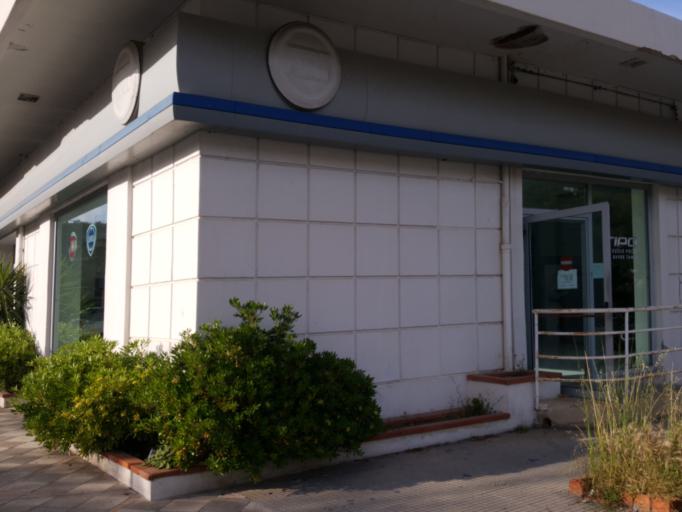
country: IT
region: Sicily
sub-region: Palermo
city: Termini Imerese
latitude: 37.9840
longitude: 13.7023
